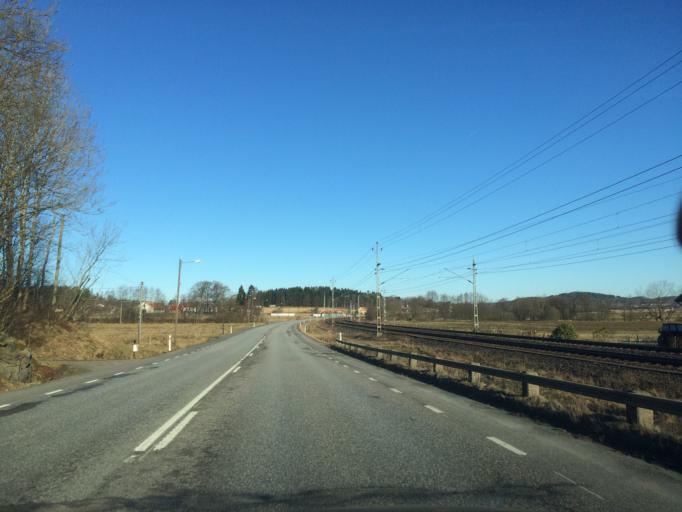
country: SE
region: Vaestra Goetaland
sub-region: Molndal
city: Lindome
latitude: 57.5554
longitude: 12.0887
